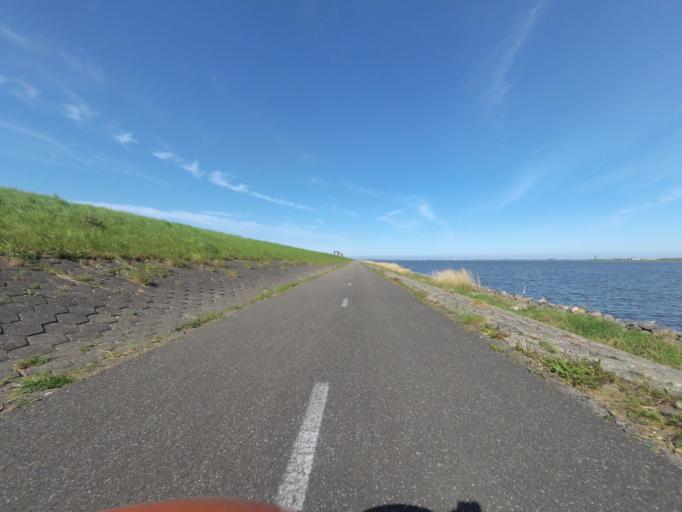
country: NL
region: Flevoland
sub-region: Gemeente Dronten
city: Dronten
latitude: 52.5826
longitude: 5.7507
